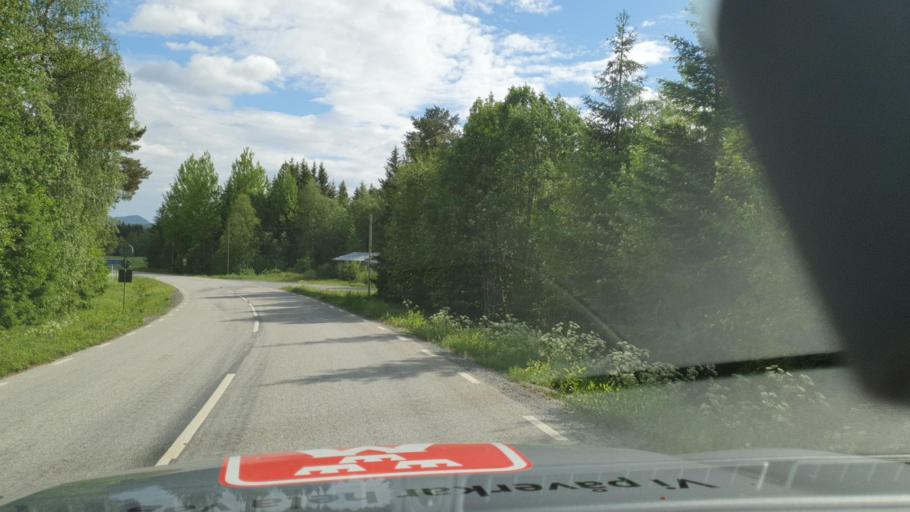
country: SE
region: Vaesternorrland
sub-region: Kramfors Kommun
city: Nordingra
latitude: 62.9025
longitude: 18.1392
